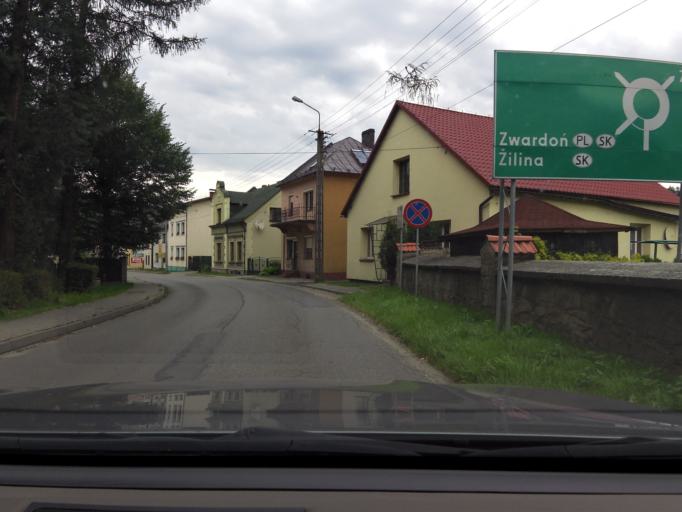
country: PL
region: Silesian Voivodeship
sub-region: Powiat zywiecki
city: Rajcza
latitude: 49.5016
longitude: 19.1012
